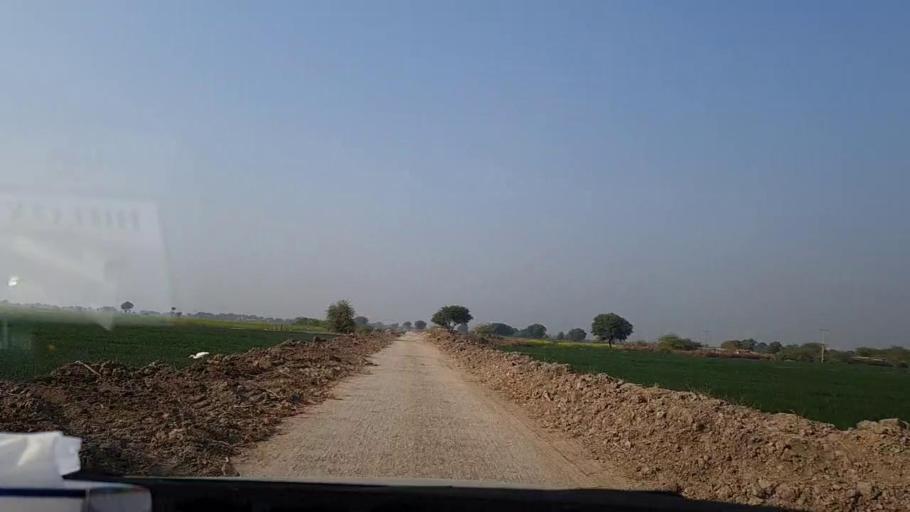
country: PK
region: Sindh
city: Tando Ghulam Ali
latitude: 25.1988
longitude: 68.8749
